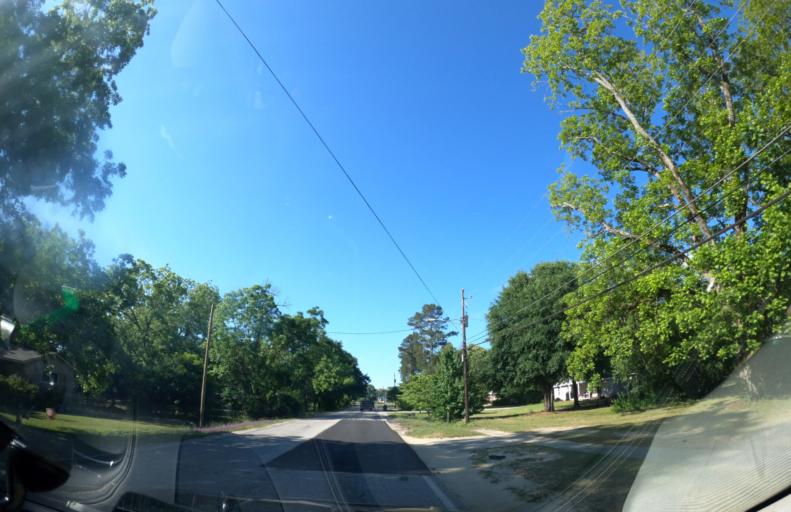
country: US
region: Georgia
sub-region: Columbia County
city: Harlem
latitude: 33.4076
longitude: -82.3145
